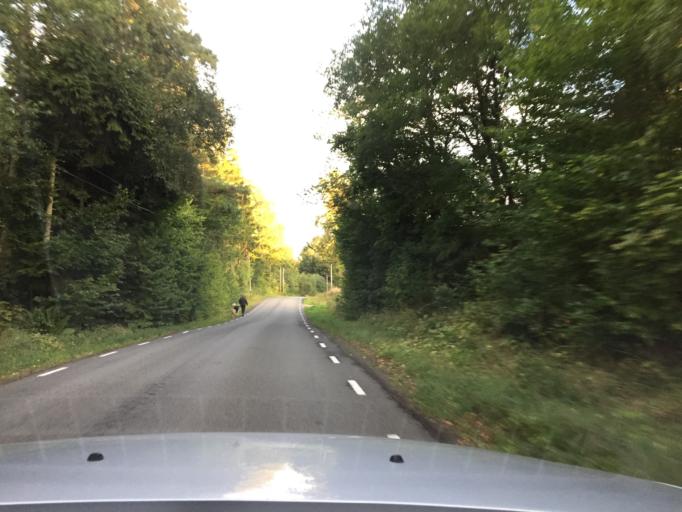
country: SE
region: Skane
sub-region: Hassleholms Kommun
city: Vinslov
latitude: 56.0348
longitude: 13.8231
